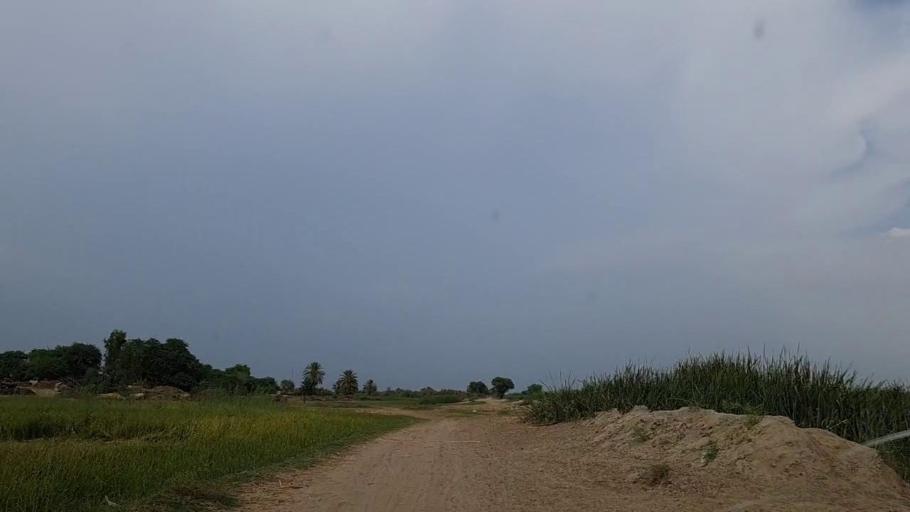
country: PK
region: Sindh
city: Khanpur
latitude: 27.8187
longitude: 69.5374
